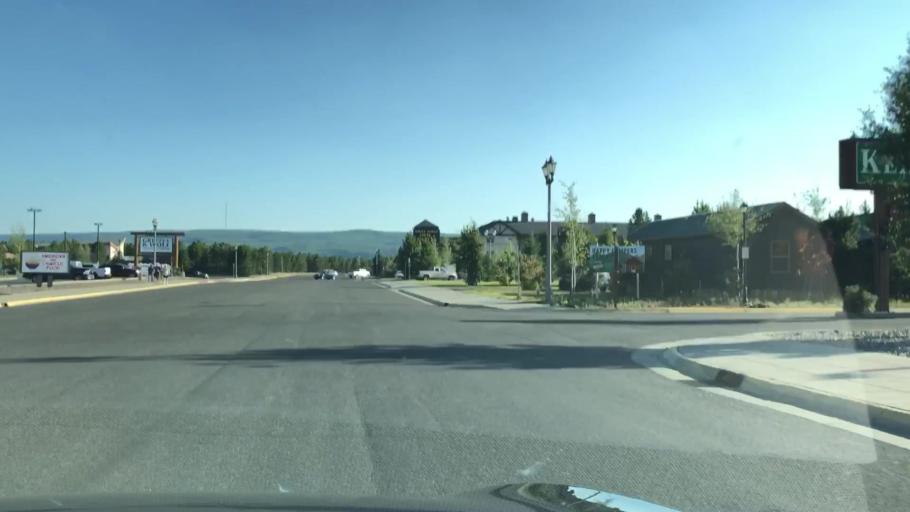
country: US
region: Montana
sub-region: Gallatin County
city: West Yellowstone
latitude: 44.6573
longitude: -111.0997
